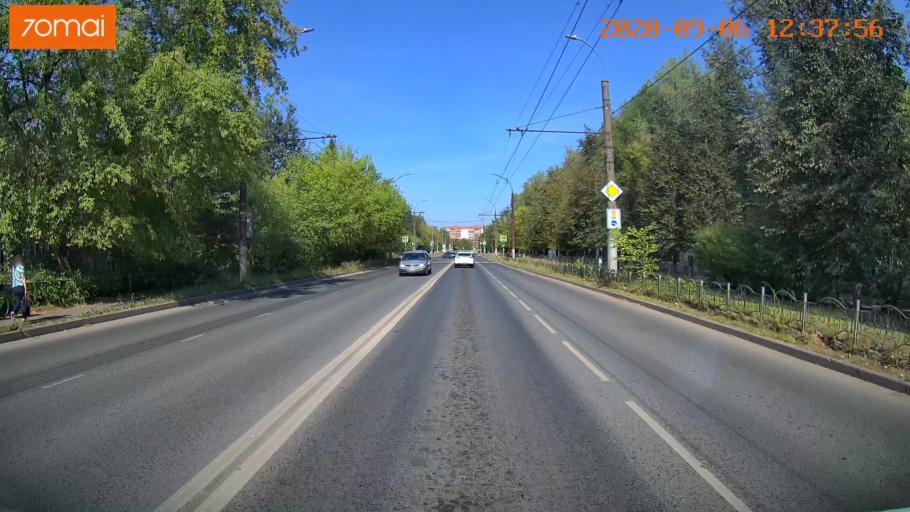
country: RU
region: Ivanovo
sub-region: Gorod Ivanovo
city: Ivanovo
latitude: 57.0294
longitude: 40.9804
